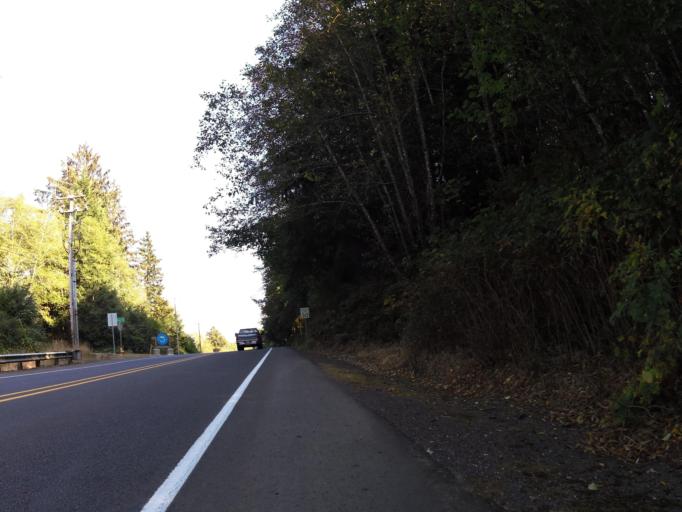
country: US
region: Oregon
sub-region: Tillamook County
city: Rockaway Beach
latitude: 45.7182
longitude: -123.9010
